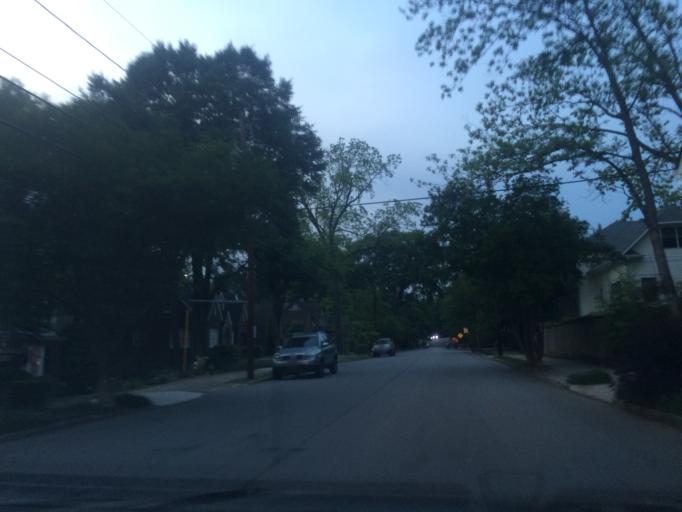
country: US
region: Georgia
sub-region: DeKalb County
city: Druid Hills
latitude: 33.7784
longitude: -84.3587
